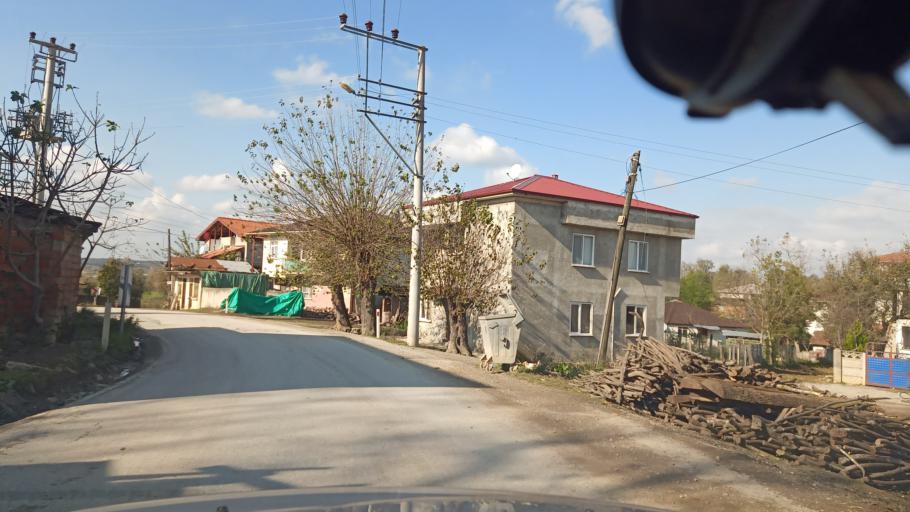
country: TR
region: Sakarya
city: Kaynarca
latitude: 41.0919
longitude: 30.4438
